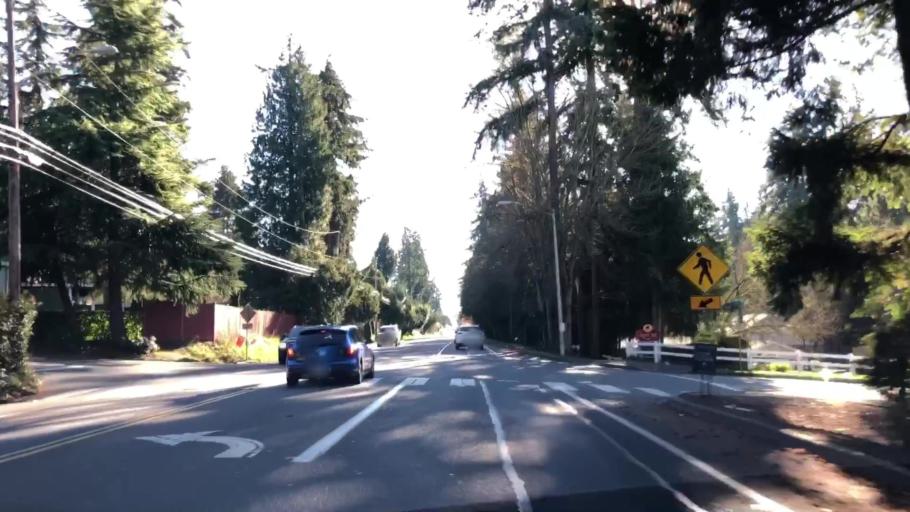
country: US
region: Washington
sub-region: King County
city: Kingsgate
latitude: 47.7015
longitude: -122.1758
